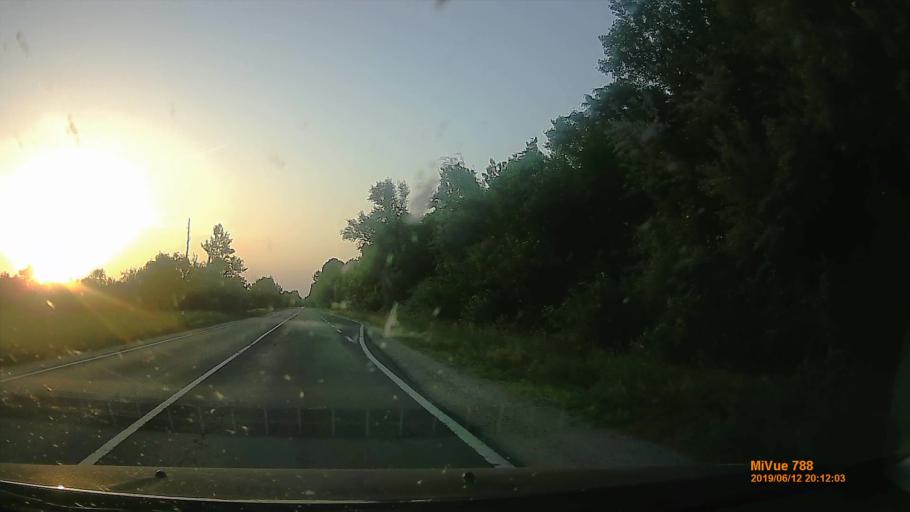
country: HU
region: Pest
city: Ocsa
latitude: 47.2831
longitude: 19.1964
